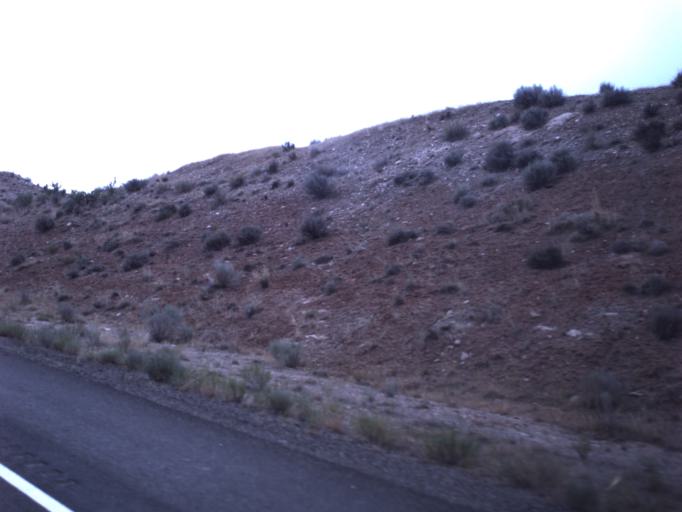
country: US
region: Utah
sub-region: Uintah County
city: Naples
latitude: 40.3035
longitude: -109.4797
